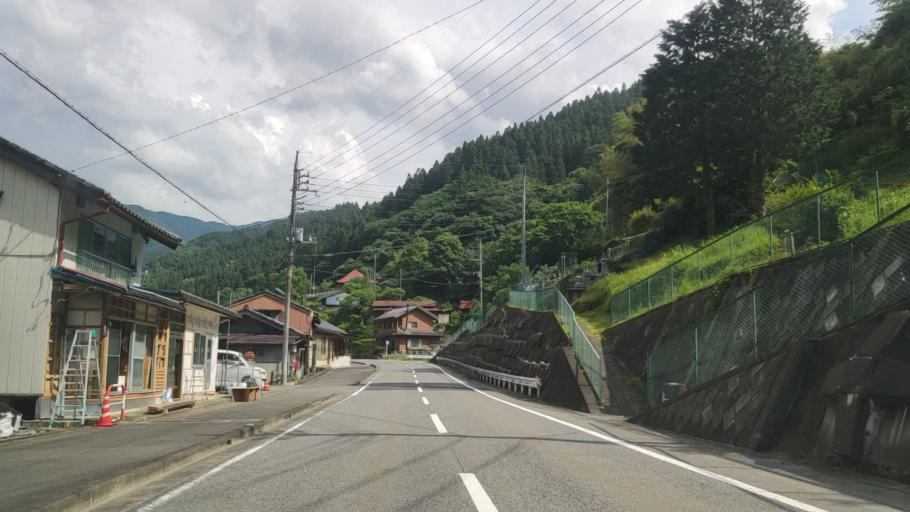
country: JP
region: Gunma
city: Tomioka
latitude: 36.1530
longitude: 138.7287
